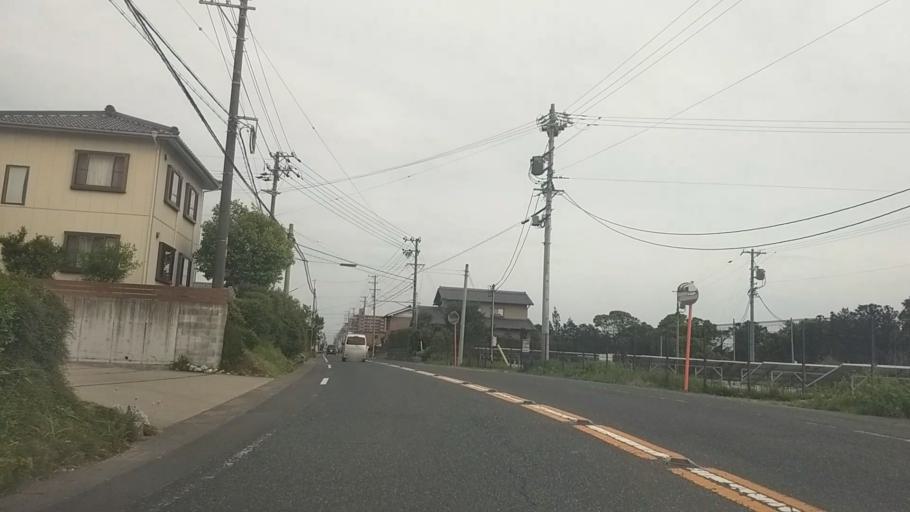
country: JP
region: Shizuoka
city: Hamamatsu
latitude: 34.7448
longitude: 137.6738
